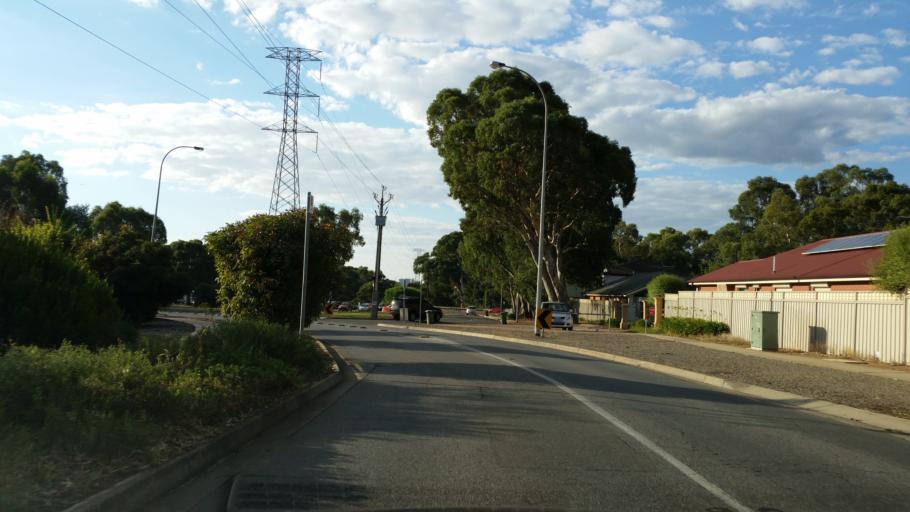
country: AU
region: South Australia
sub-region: Marion
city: Trott Park
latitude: -35.0859
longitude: 138.5844
